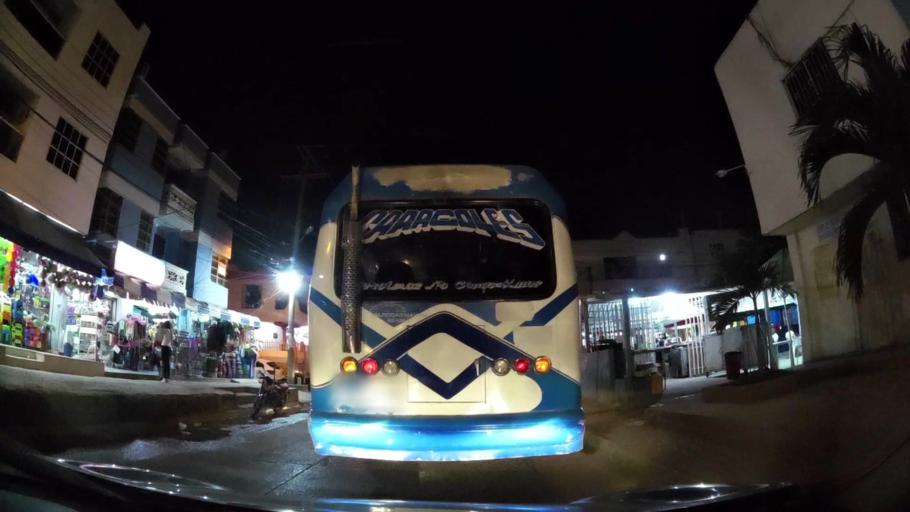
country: CO
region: Bolivar
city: Cartagena
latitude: 10.3810
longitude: -75.4964
